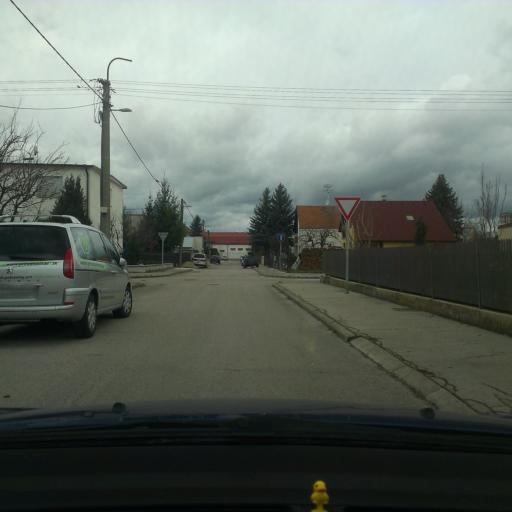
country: SK
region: Trnavsky
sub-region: Okres Trnava
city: Piestany
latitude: 48.5942
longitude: 17.8180
